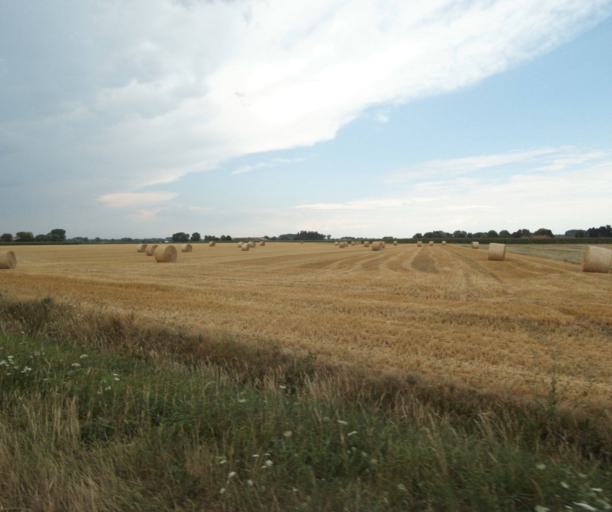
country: FR
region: Nord-Pas-de-Calais
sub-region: Departement du Nord
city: Deulemont
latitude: 50.7330
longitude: 2.9614
